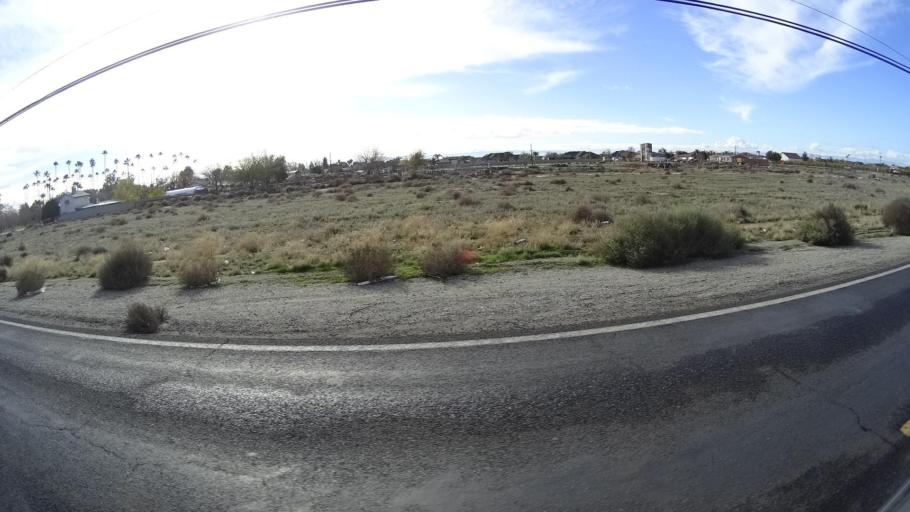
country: US
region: California
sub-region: Kern County
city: Rosedale
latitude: 35.3840
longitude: -119.1912
